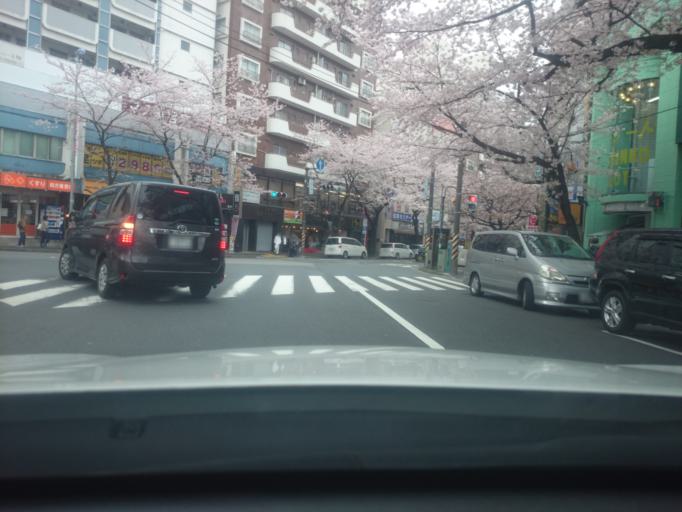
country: JP
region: Tokyo
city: Chofugaoka
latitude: 35.5786
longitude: 139.5733
